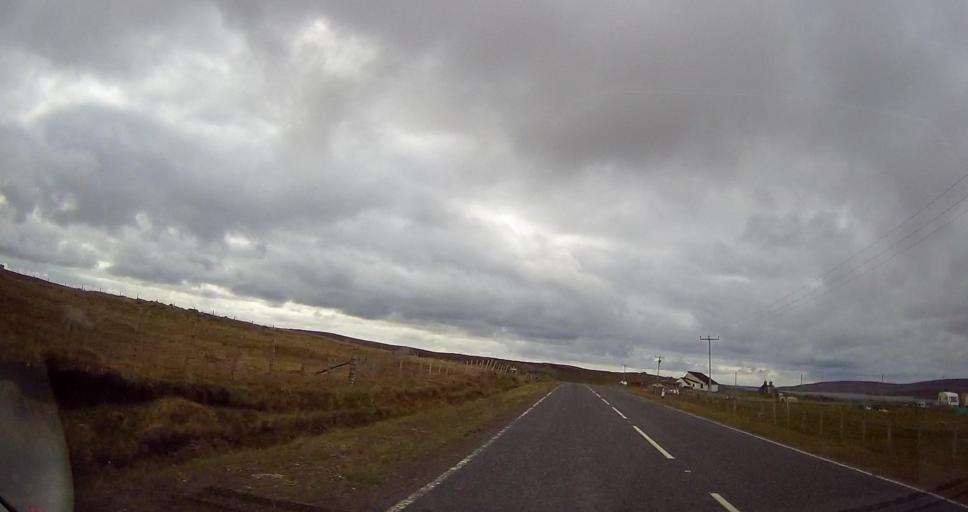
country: GB
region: Scotland
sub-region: Shetland Islands
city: Shetland
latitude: 60.6657
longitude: -1.0579
